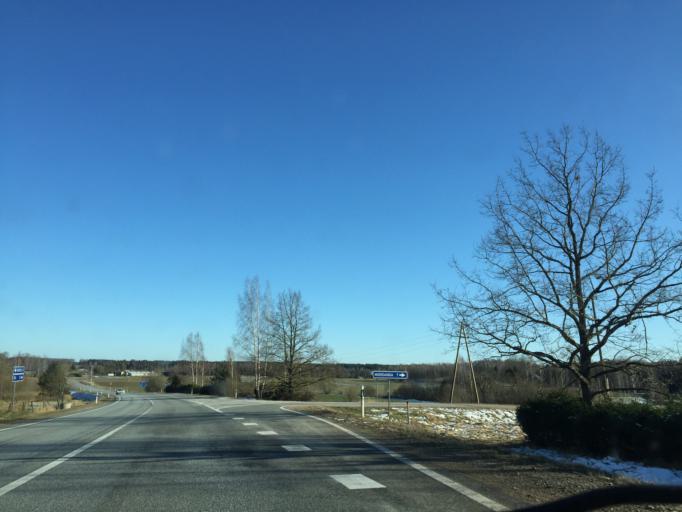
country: LV
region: Talsu Rajons
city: Stende
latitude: 57.2085
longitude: 22.2865
